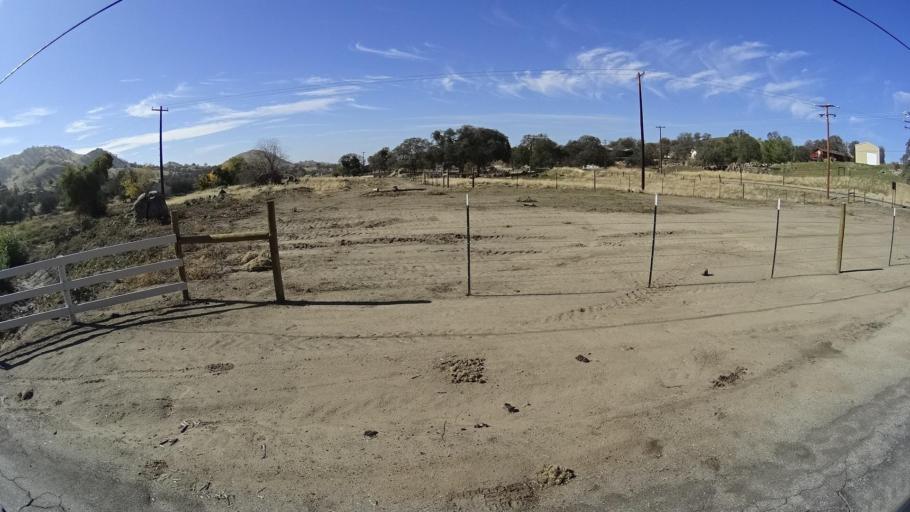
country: US
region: California
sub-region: Kern County
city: Alta Sierra
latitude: 35.7037
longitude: -118.8345
